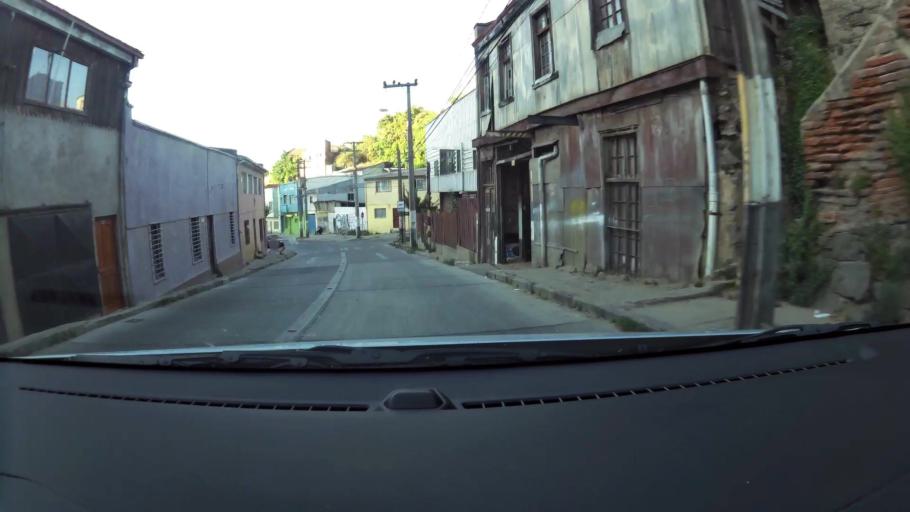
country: CL
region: Valparaiso
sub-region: Provincia de Valparaiso
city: Valparaiso
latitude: -33.0548
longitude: -71.6065
